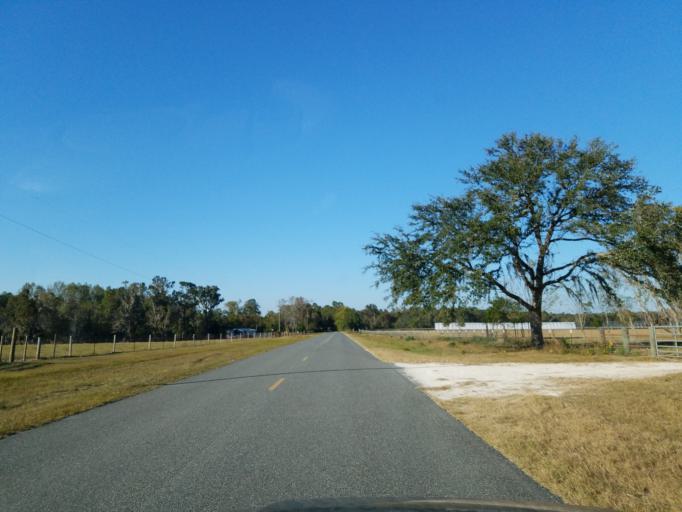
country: US
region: Georgia
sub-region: Echols County
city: Statenville
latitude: 30.6164
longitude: -83.0963
